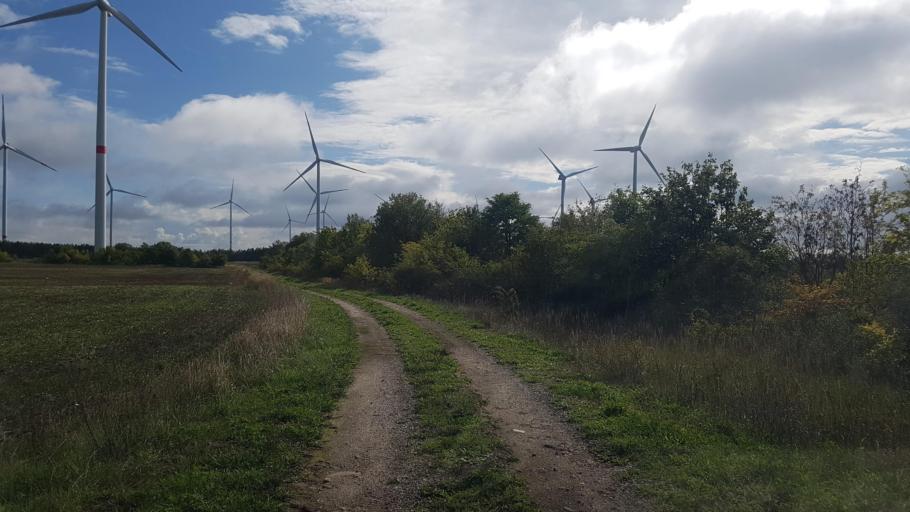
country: DE
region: Brandenburg
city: Sallgast
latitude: 51.5566
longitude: 13.8348
